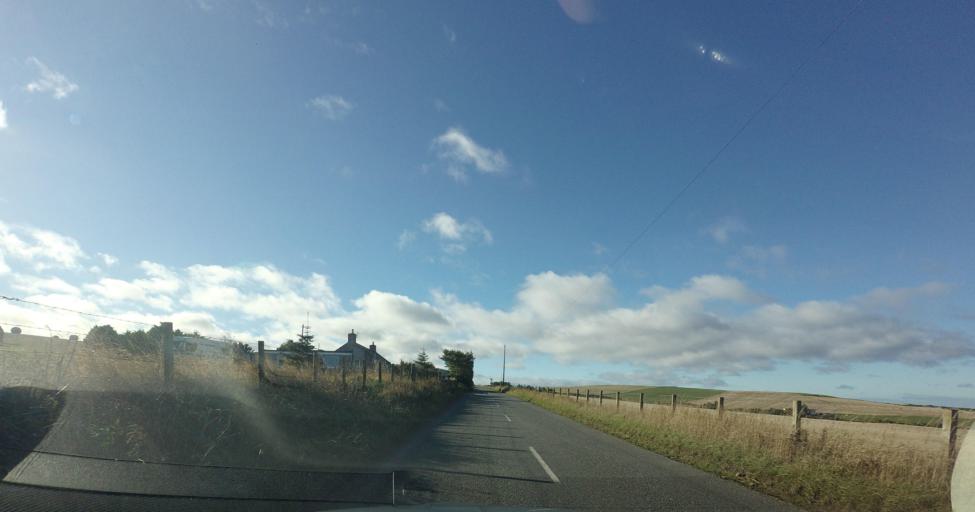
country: GB
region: Scotland
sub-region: Aberdeenshire
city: Macduff
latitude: 57.6671
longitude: -2.3094
